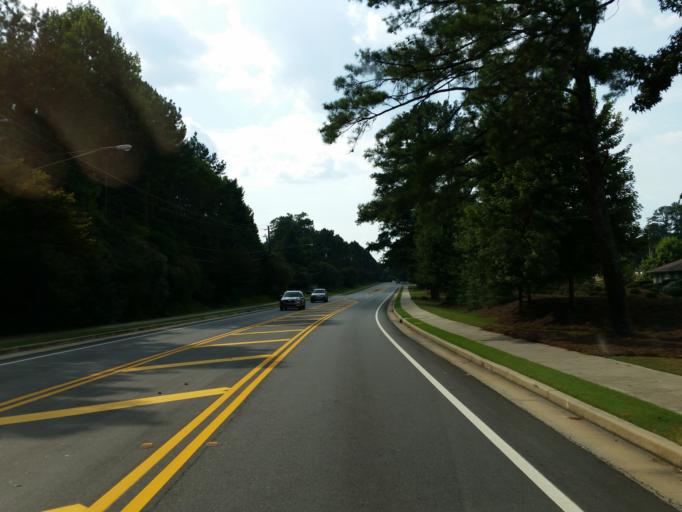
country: US
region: Georgia
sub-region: Fulton County
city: Roswell
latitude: 34.0478
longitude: -84.3773
